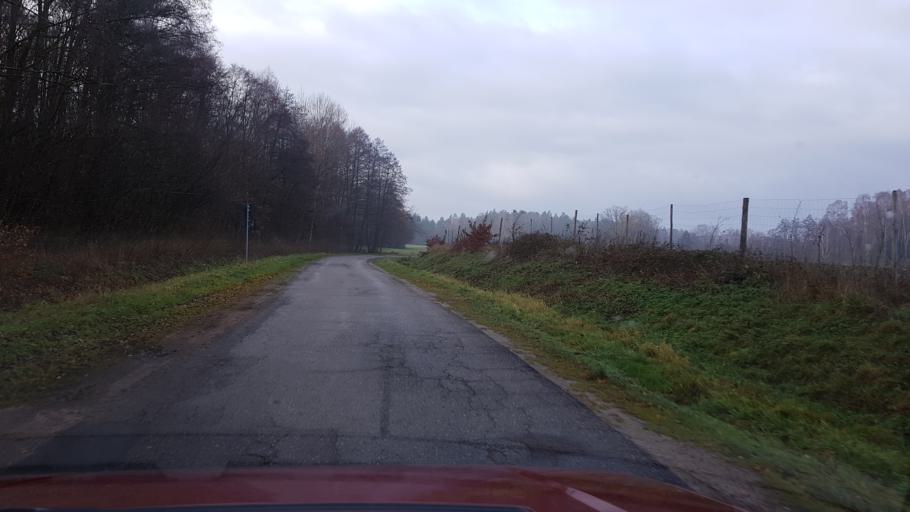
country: PL
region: West Pomeranian Voivodeship
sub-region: Powiat bialogardzki
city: Tychowo
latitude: 53.9458
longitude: 16.3188
